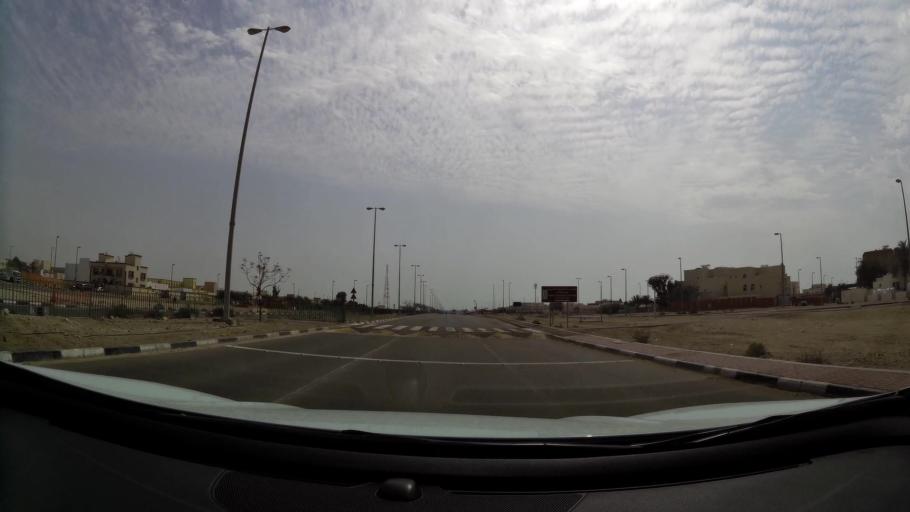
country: AE
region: Abu Dhabi
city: Abu Dhabi
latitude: 24.5569
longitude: 54.6856
